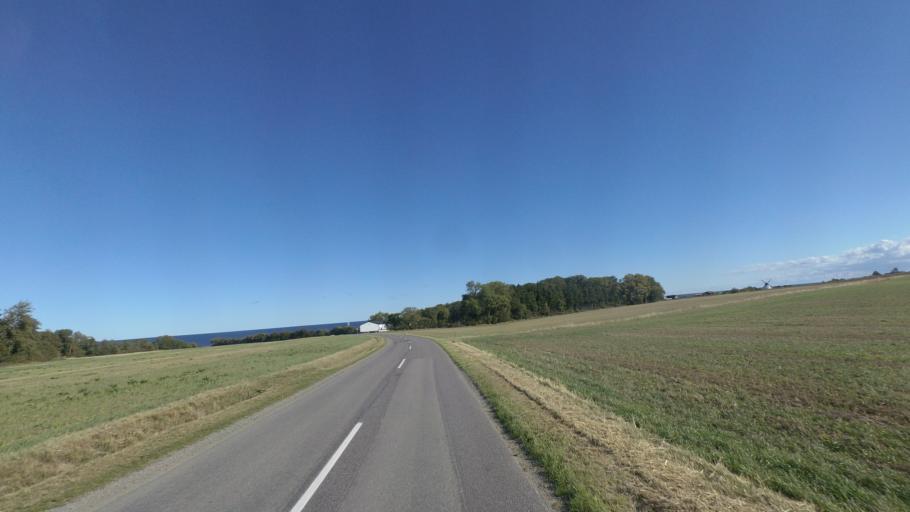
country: DK
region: Capital Region
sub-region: Bornholm Kommune
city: Nexo
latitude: 55.1103
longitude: 15.1343
